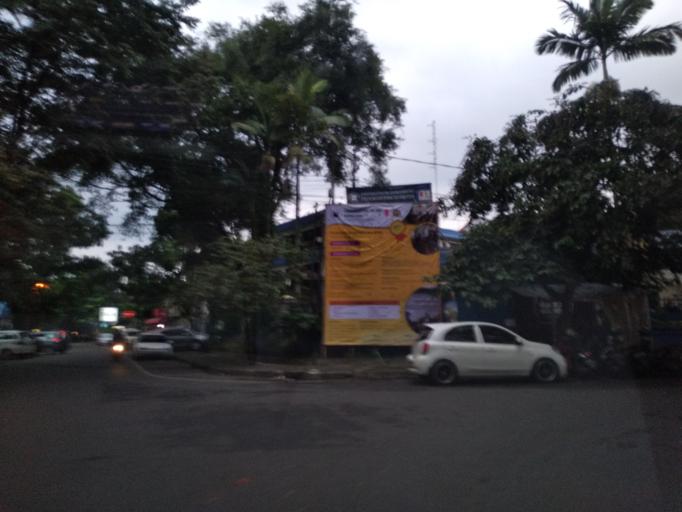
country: ID
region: West Java
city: Bandung
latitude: -6.9029
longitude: 107.6112
